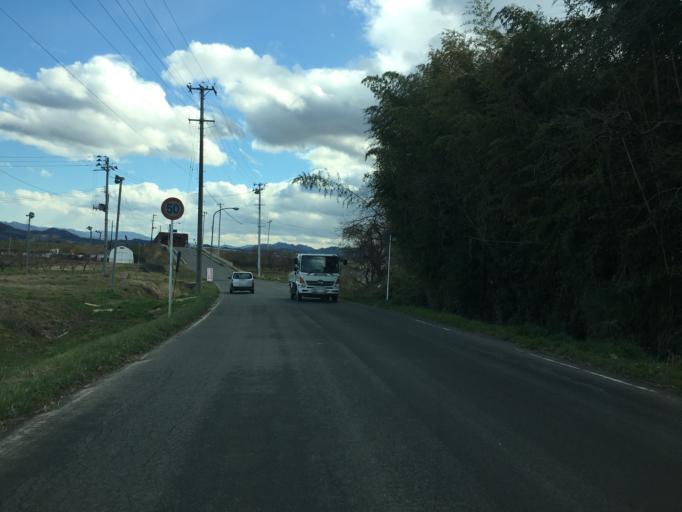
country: JP
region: Fukushima
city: Yanagawamachi-saiwaicho
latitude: 37.8657
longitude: 140.5682
